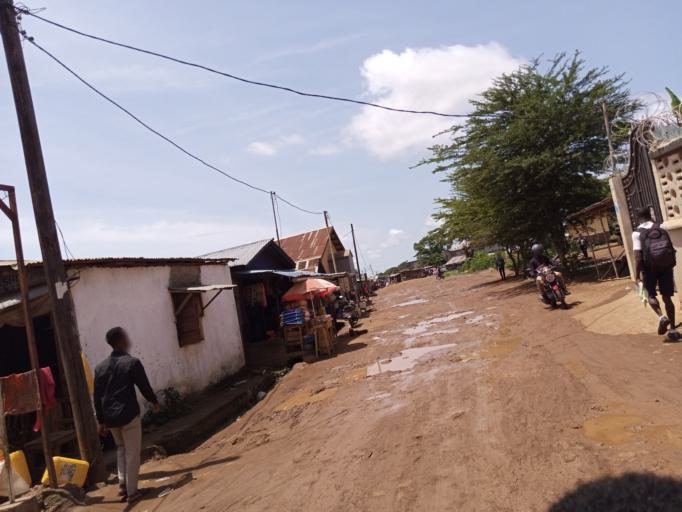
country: SL
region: Western Area
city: Hastings
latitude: 8.3851
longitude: -13.1370
